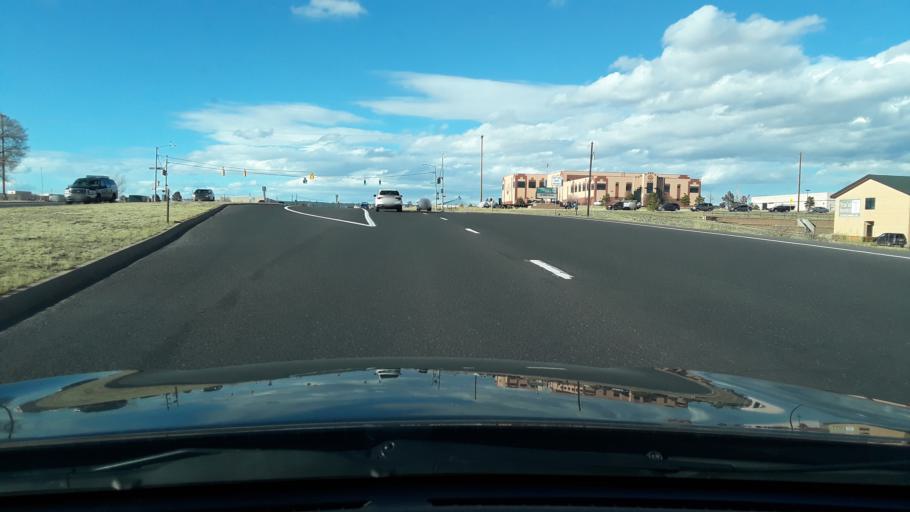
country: US
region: Colorado
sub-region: El Paso County
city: Air Force Academy
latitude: 38.9790
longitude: -104.7978
